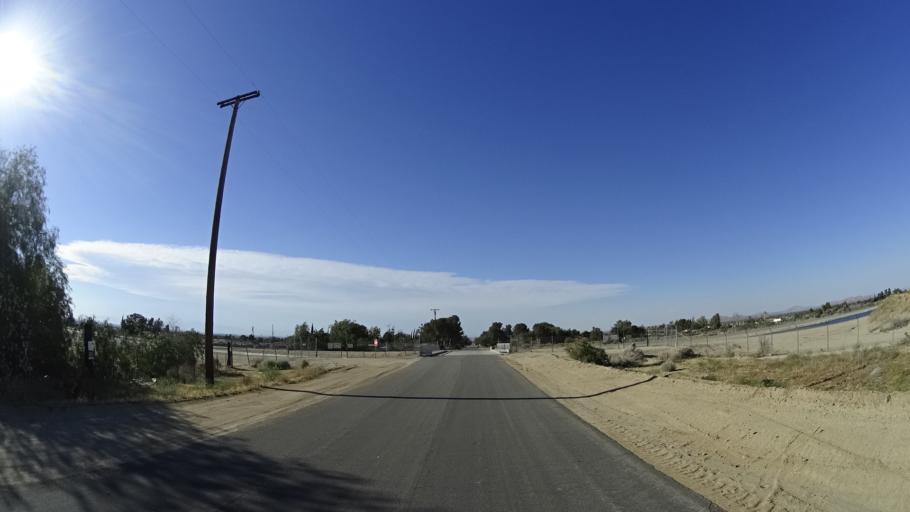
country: US
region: California
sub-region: Los Angeles County
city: Littlerock
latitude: 34.5166
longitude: -117.9924
